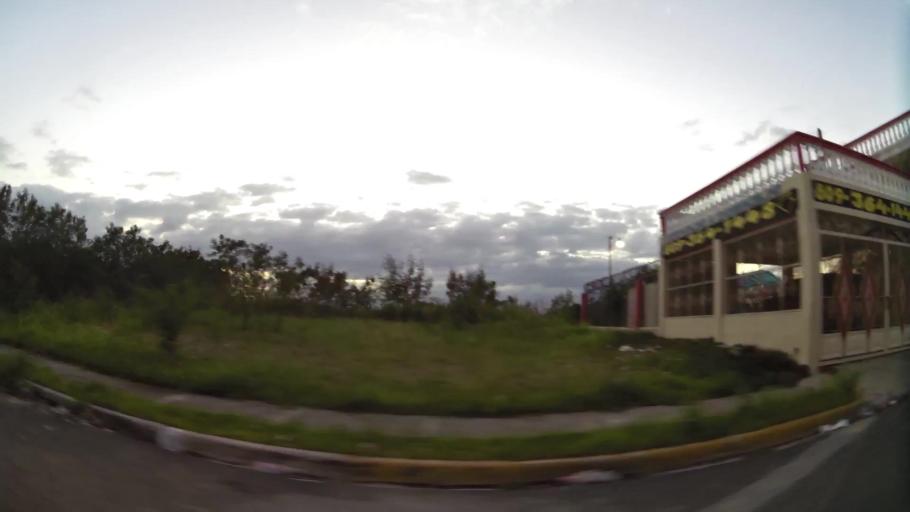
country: DO
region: Nacional
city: La Agustina
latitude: 18.5452
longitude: -69.9438
